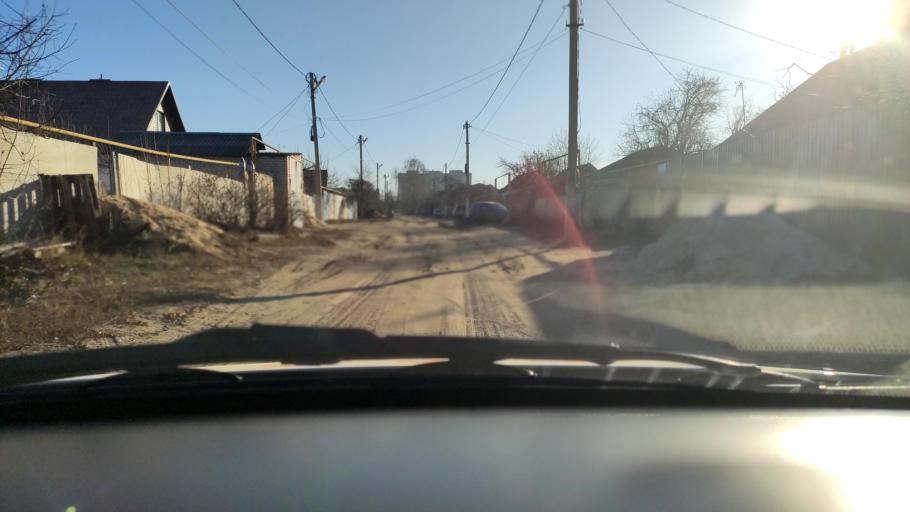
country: RU
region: Voronezj
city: Podgornoye
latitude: 51.7306
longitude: 39.1552
